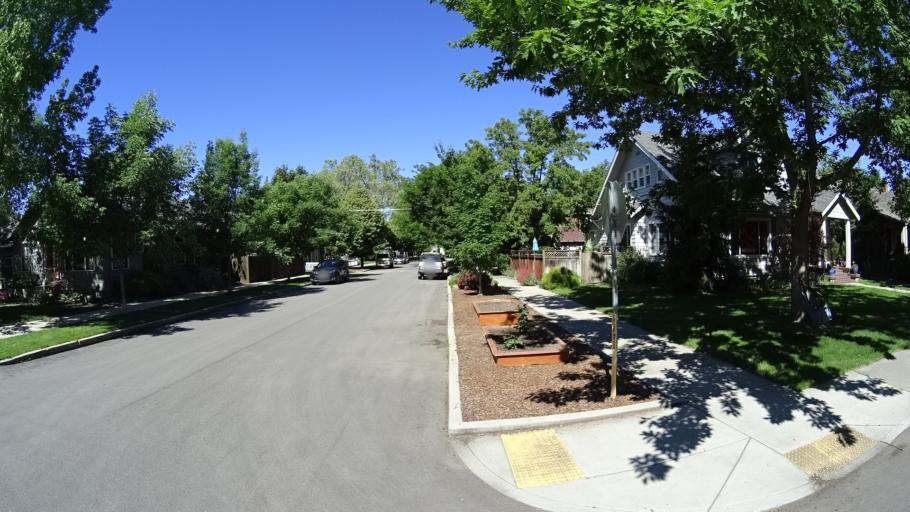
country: US
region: Idaho
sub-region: Ada County
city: Boise
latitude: 43.6303
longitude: -116.2134
